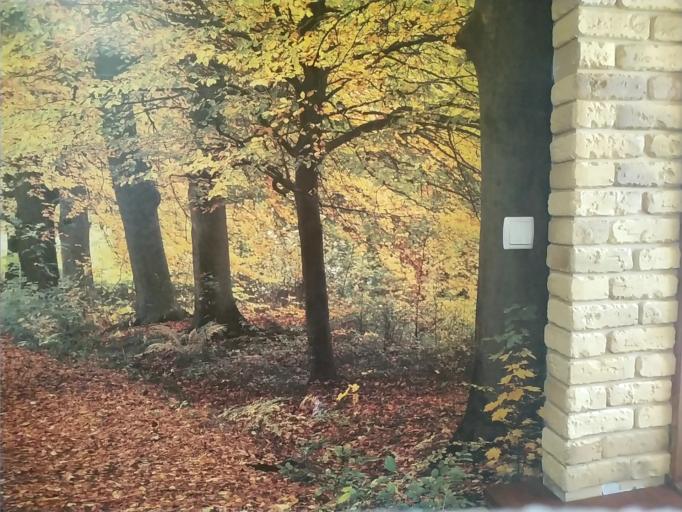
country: RU
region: Tverskaya
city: Vyshniy Volochek
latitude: 57.6072
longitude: 34.6006
